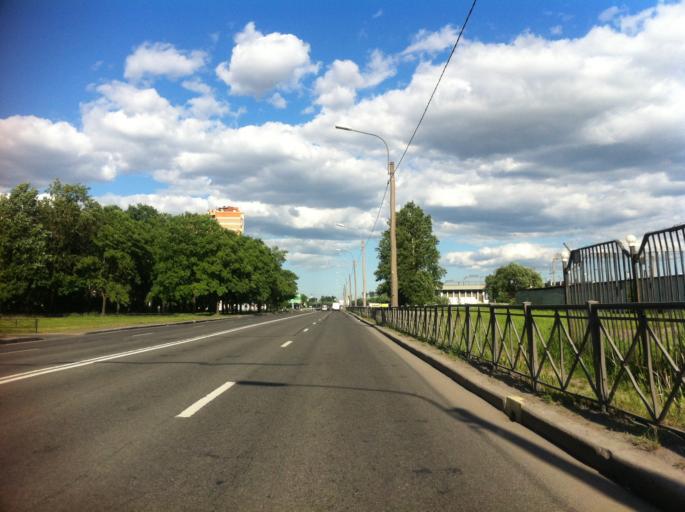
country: RU
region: St.-Petersburg
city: Dachnoye
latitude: 59.8248
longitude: 30.2167
